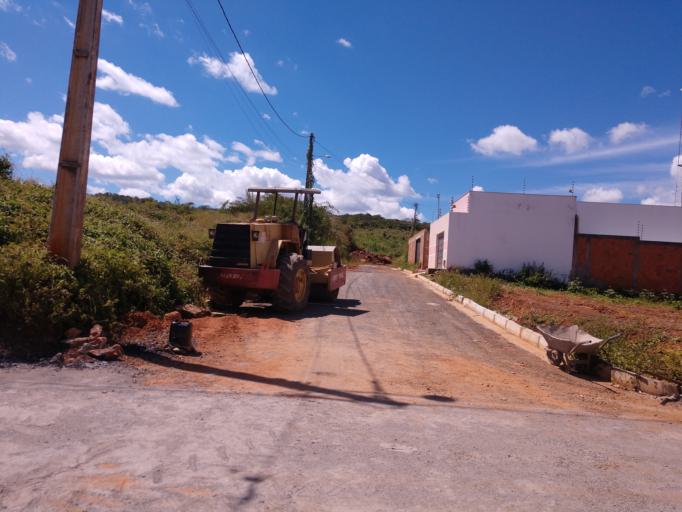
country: BR
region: Bahia
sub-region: Sao Desiderio
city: Sao Desiderio
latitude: -12.3569
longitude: -44.9712
